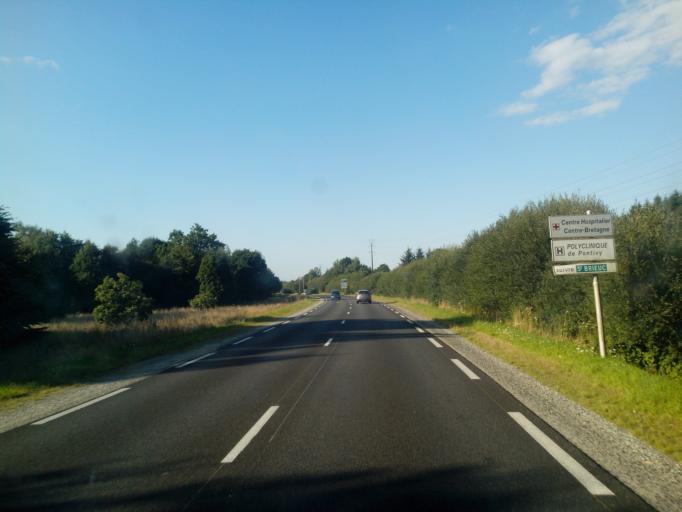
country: FR
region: Brittany
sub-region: Departement du Morbihan
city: Saint-Thuriau
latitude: 48.0473
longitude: -2.9456
